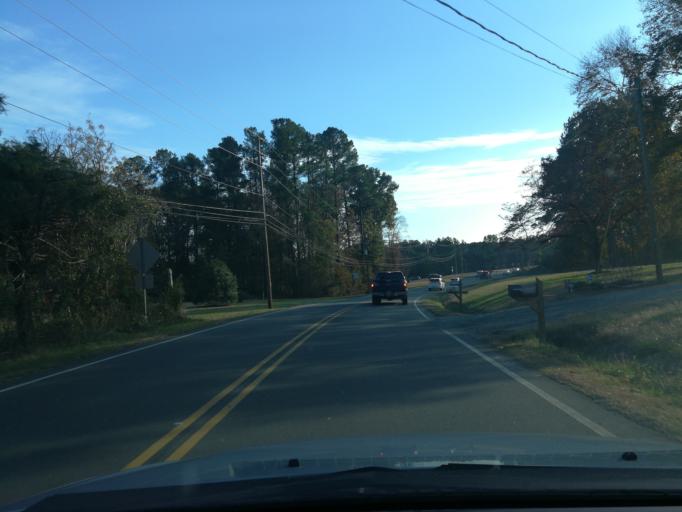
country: US
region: North Carolina
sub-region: Orange County
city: Chapel Hill
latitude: 35.9703
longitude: -79.0075
